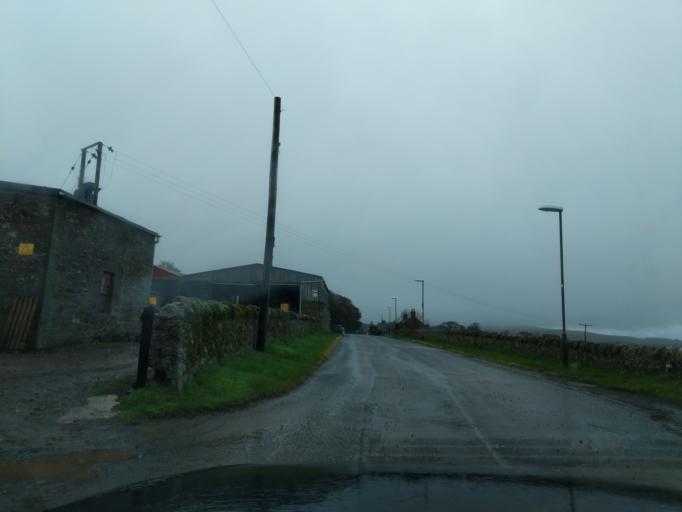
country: GB
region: Scotland
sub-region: East Lothian
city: Dunbar
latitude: 55.9569
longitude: -2.4419
